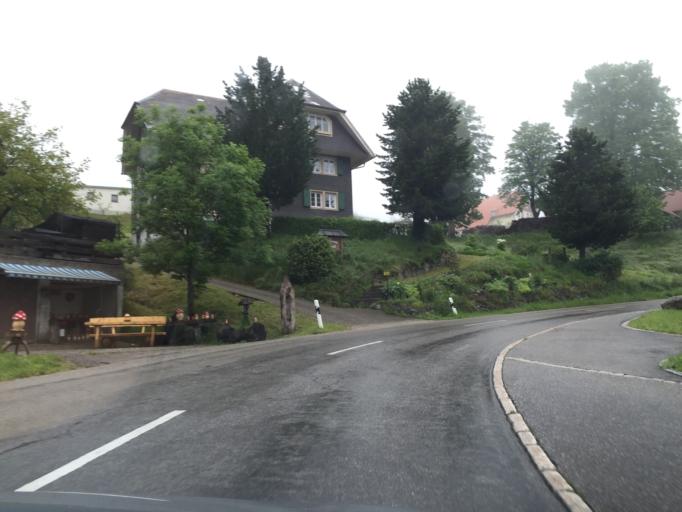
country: DE
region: Baden-Wuerttemberg
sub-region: Freiburg Region
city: Todtnau
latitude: 47.8492
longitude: 7.9378
